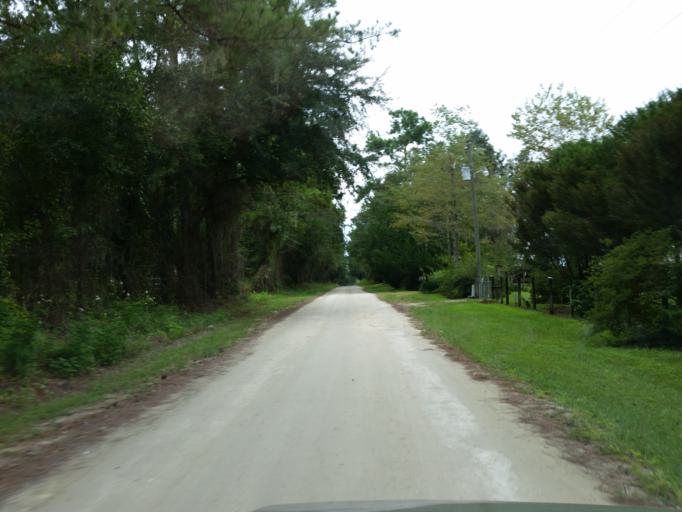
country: US
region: Florida
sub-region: Alachua County
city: High Springs
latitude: 29.9527
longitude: -82.5594
